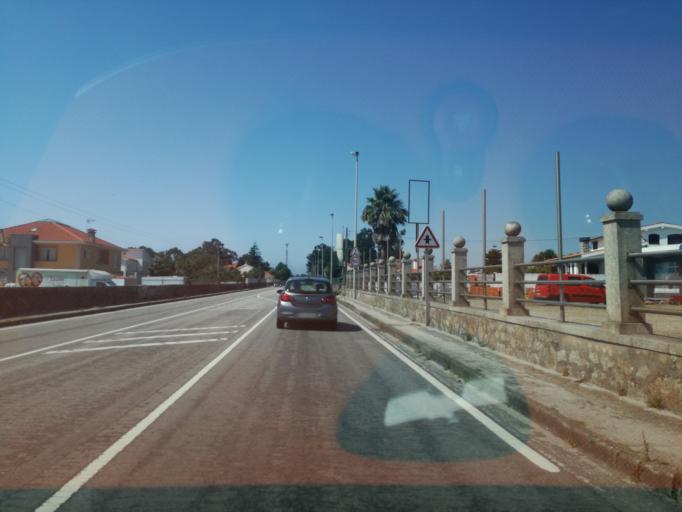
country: PT
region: Braga
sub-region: Esposende
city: Esposende
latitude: 41.5340
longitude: -8.7775
